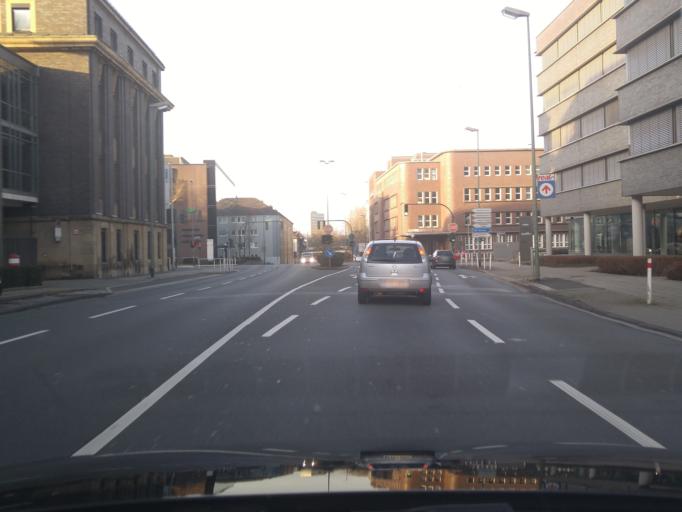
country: DE
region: North Rhine-Westphalia
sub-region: Regierungsbezirk Dusseldorf
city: Essen
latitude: 51.4460
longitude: 7.0213
